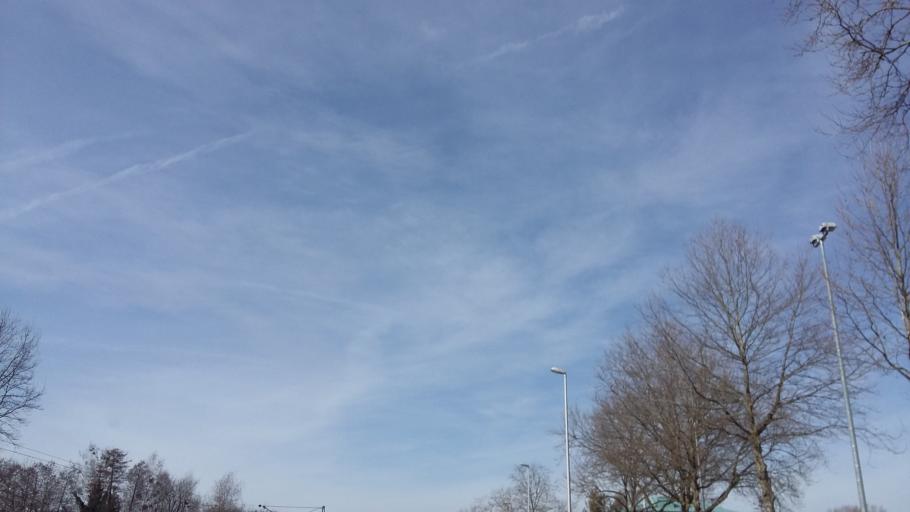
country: AT
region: Vorarlberg
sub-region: Politischer Bezirk Bregenz
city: Horbranz
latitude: 47.5489
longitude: 9.7228
